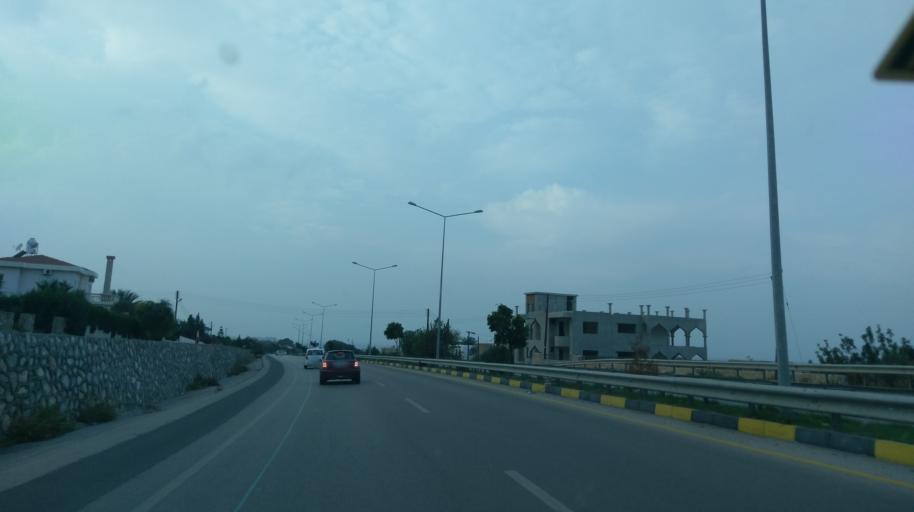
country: CY
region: Keryneia
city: Kyrenia
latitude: 35.3390
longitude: 33.2543
